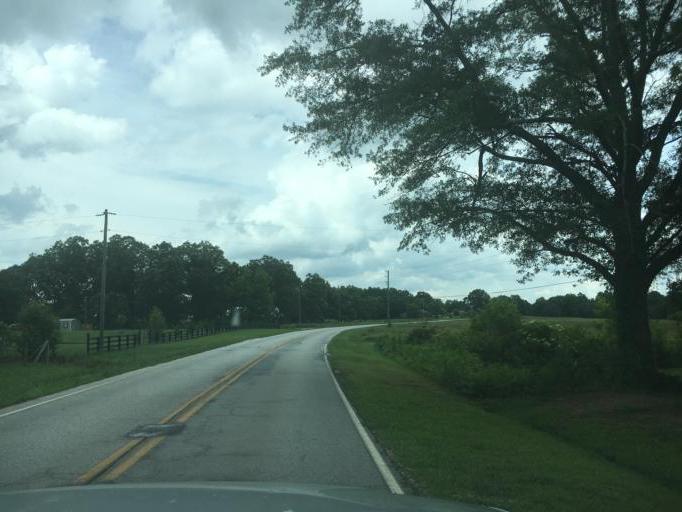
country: US
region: Georgia
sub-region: Hart County
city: Reed Creek
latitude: 34.4269
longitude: -82.9826
